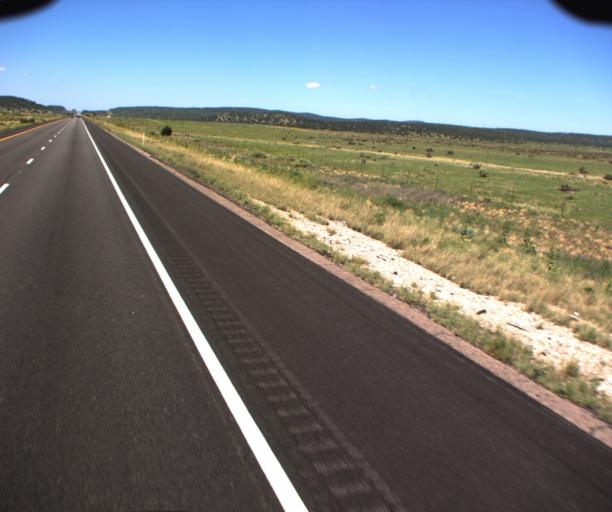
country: US
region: Arizona
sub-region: Mohave County
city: Peach Springs
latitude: 35.2622
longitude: -113.1607
